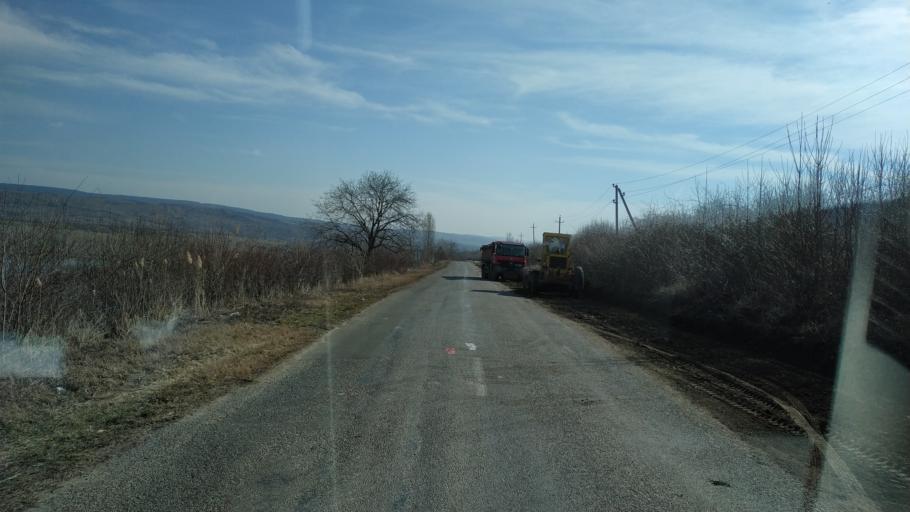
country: MD
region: Nisporeni
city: Nisporeni
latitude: 47.1827
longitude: 28.0768
